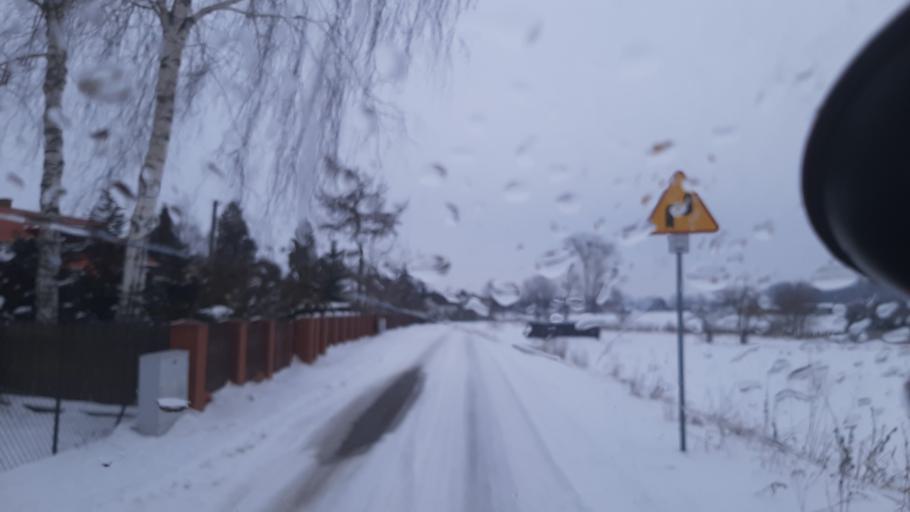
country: PL
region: Lublin Voivodeship
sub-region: Powiat lubelski
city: Garbow
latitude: 51.3582
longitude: 22.3780
